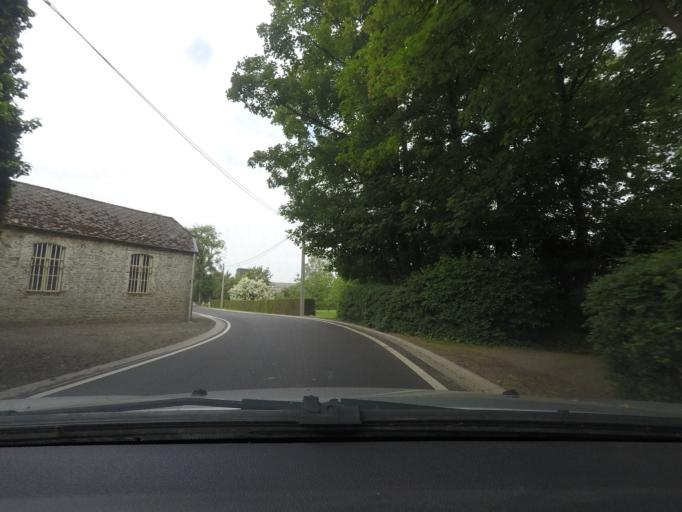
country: BE
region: Wallonia
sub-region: Province de Namur
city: Noville-les-Bois
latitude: 50.4925
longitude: 5.0071
